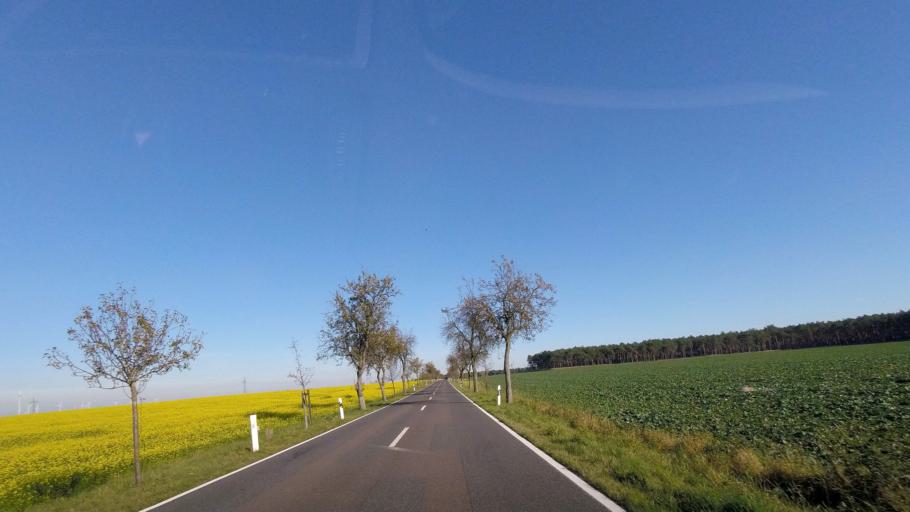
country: DE
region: Saxony-Anhalt
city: Zahna
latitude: 51.9729
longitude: 12.8079
